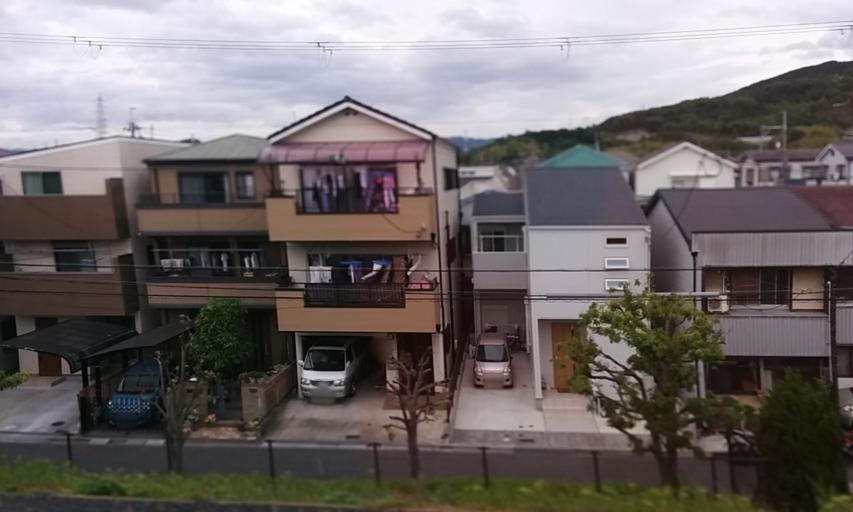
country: JP
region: Osaka
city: Takatsuki
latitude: 34.8570
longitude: 135.6381
